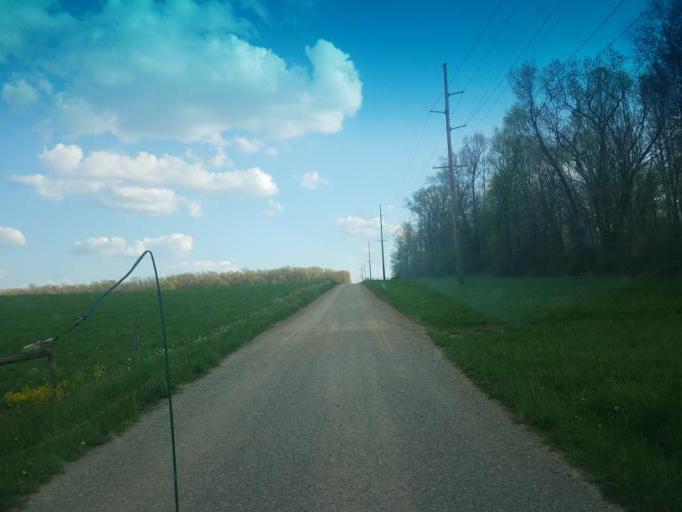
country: US
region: Ohio
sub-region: Wayne County
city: Shreve
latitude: 40.6438
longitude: -82.0337
